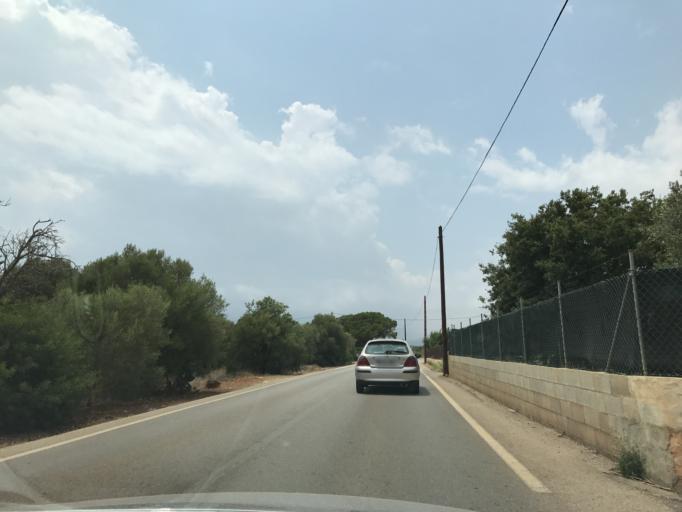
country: ES
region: Balearic Islands
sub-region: Illes Balears
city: Son Servera
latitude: 39.5704
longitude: 3.3657
